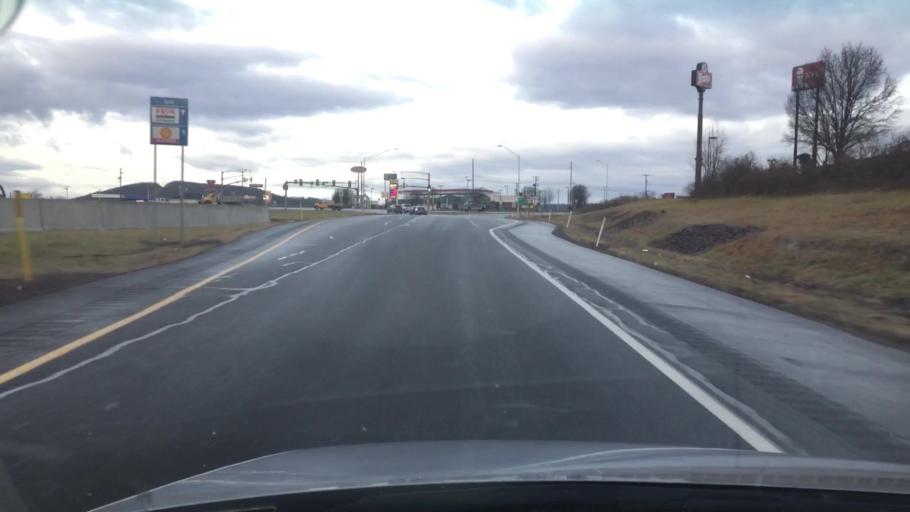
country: US
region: Pennsylvania
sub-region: Columbia County
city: Bloomsburg
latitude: 41.0147
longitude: -76.4889
